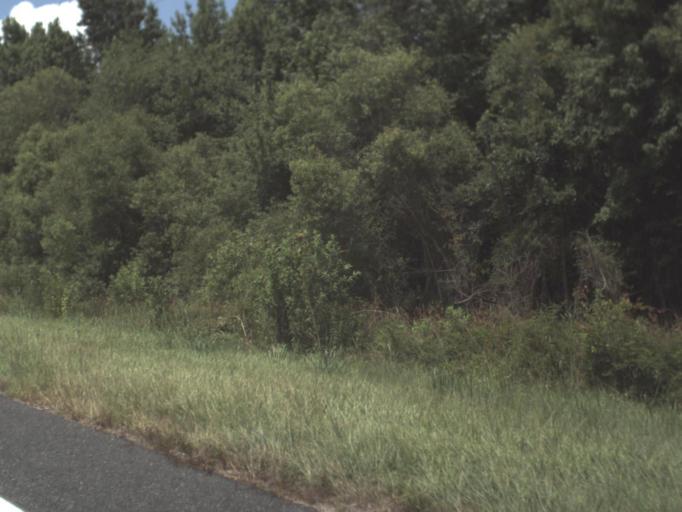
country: US
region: Florida
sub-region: Taylor County
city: Perry
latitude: 30.2680
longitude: -83.7160
